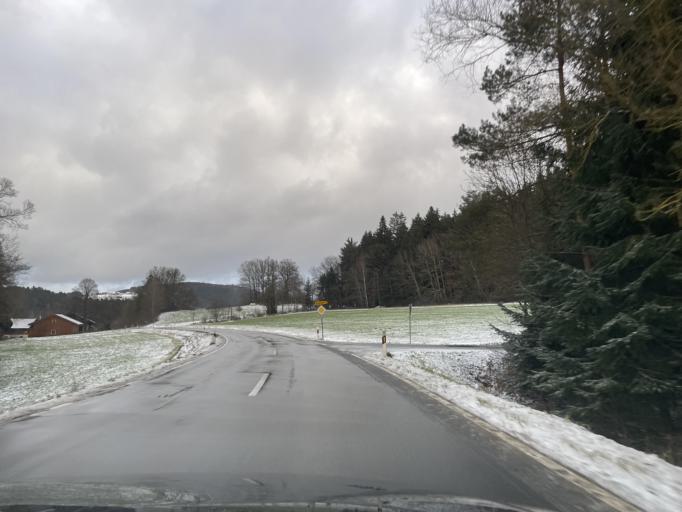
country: DE
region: Bavaria
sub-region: Lower Bavaria
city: Prackenbach
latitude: 49.1009
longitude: 12.8390
